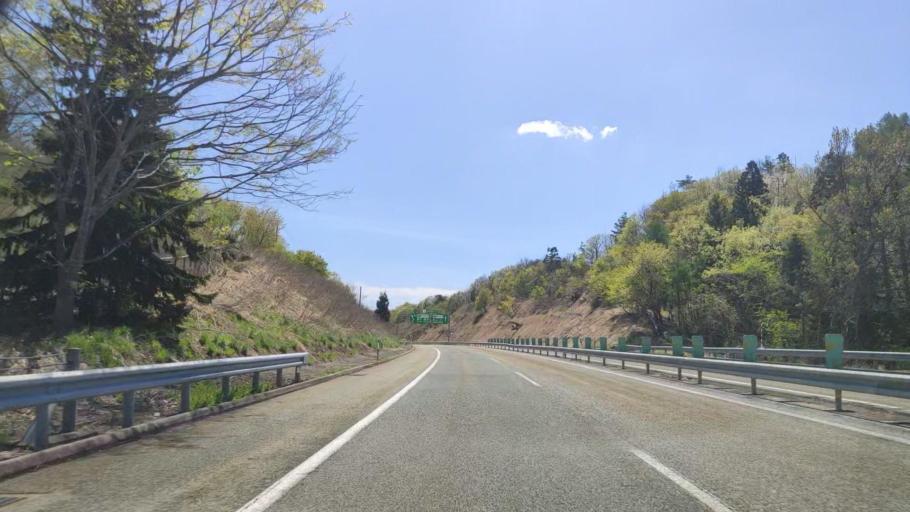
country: JP
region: Akita
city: Yokotemachi
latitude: 39.2842
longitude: 140.5317
